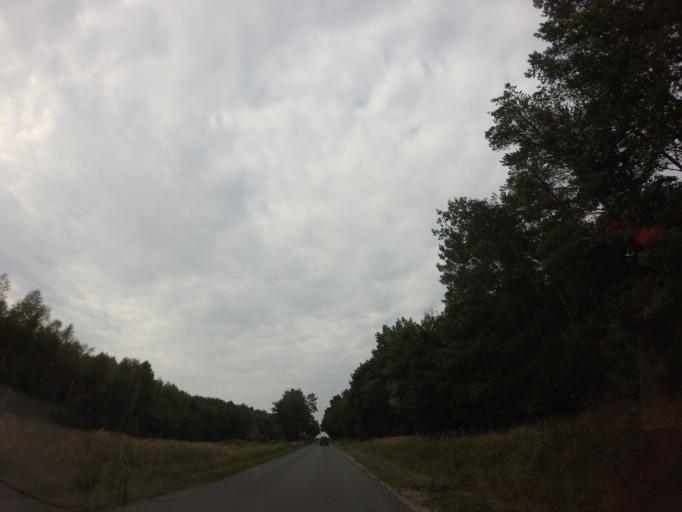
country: PL
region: West Pomeranian Voivodeship
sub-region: Powiat drawski
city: Drawsko Pomorskie
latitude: 53.5059
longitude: 15.7857
